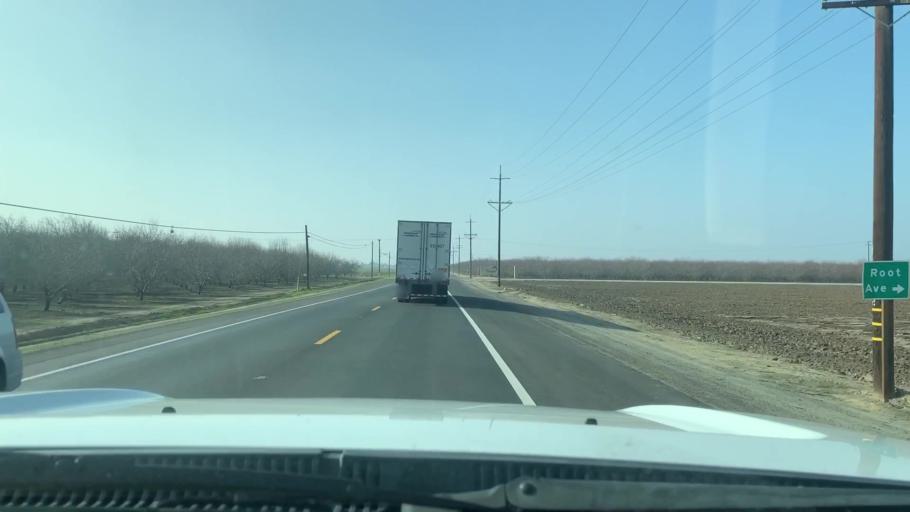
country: US
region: California
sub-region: Kern County
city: Wasco
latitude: 35.6017
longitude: -119.3104
